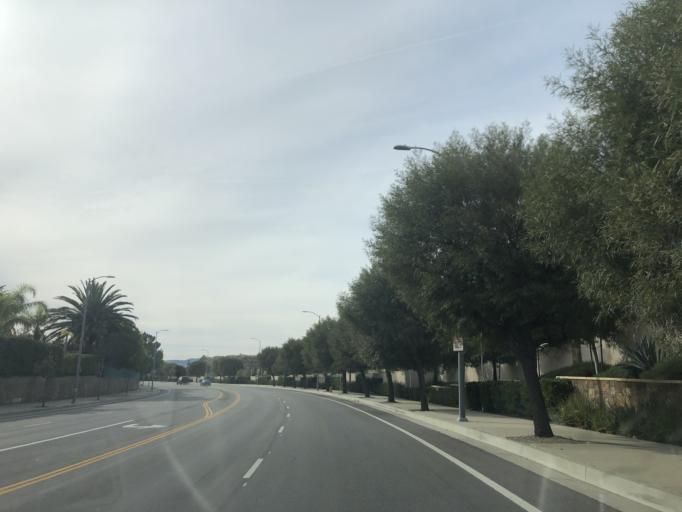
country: US
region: California
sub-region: Los Angeles County
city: Chatsworth
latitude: 34.2692
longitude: -118.5636
